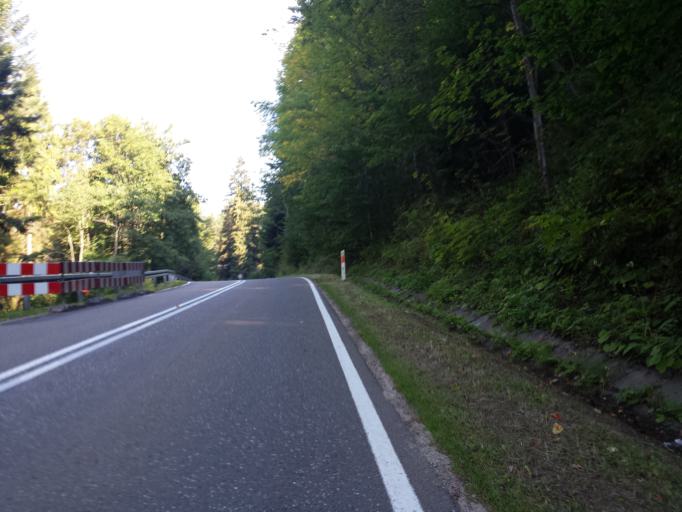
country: PL
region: Subcarpathian Voivodeship
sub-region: Powiat leski
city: Cisna
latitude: 49.2222
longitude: 22.3121
